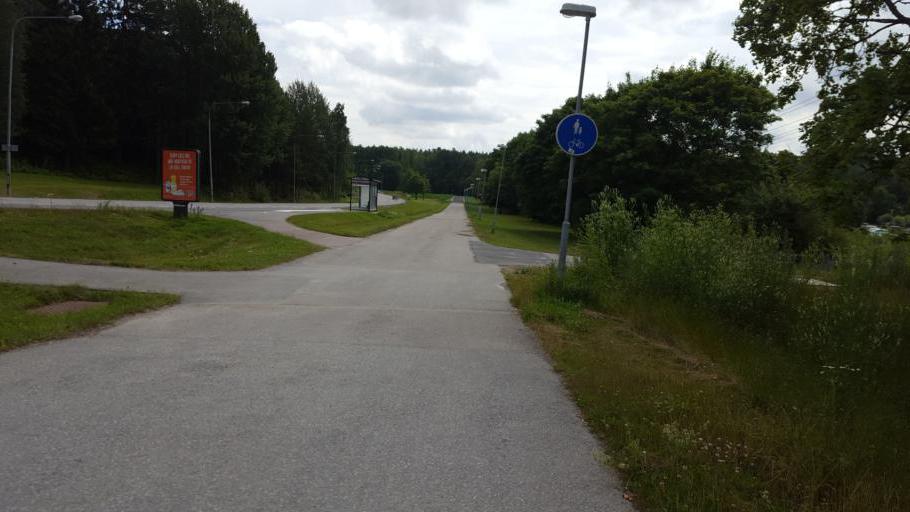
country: SE
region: Stockholm
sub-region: Upplands Vasby Kommun
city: Upplands Vaesby
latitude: 59.5097
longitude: 17.9000
